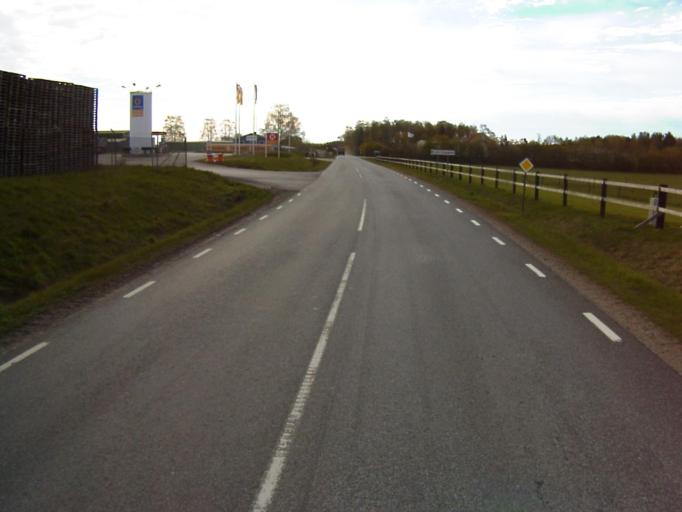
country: SE
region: Skane
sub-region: Kristianstads Kommun
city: Norra Asum
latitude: 55.9940
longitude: 14.1165
